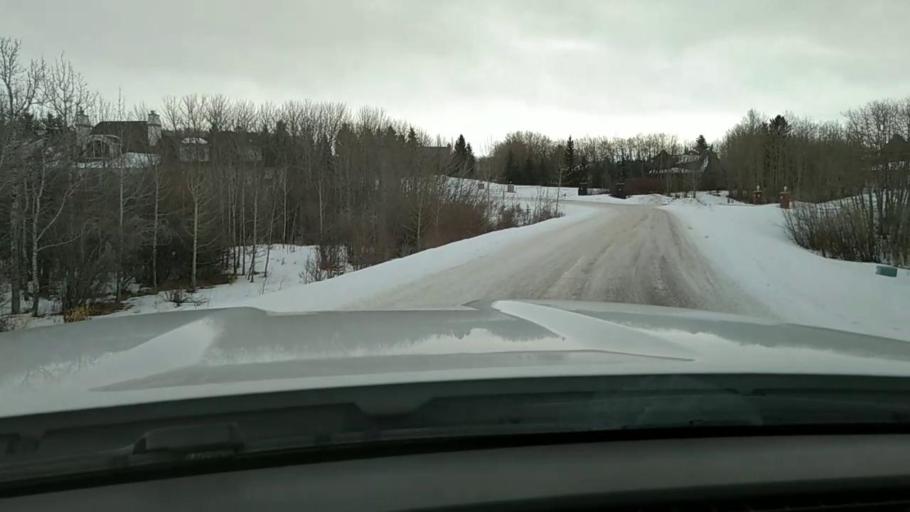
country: CA
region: Alberta
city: Calgary
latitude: 51.1556
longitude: -114.2574
